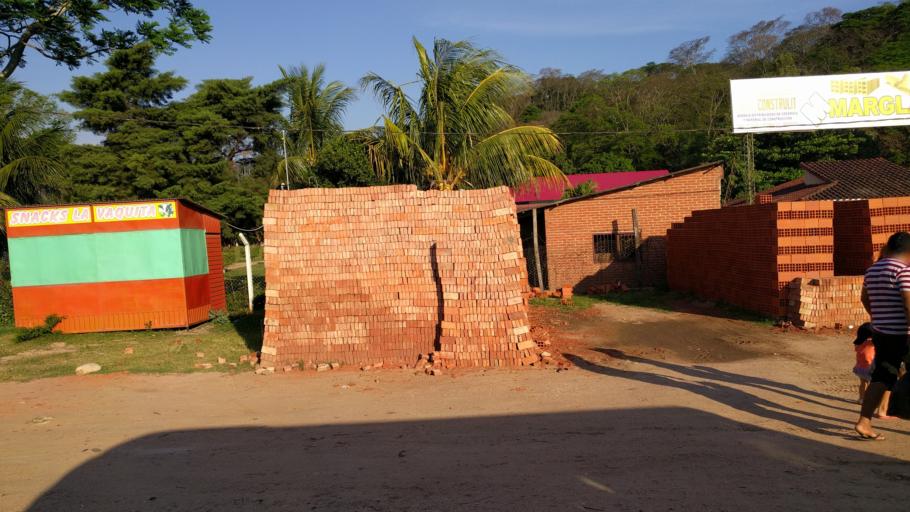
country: BO
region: Santa Cruz
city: Santiago del Torno
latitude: -18.0063
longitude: -63.3903
